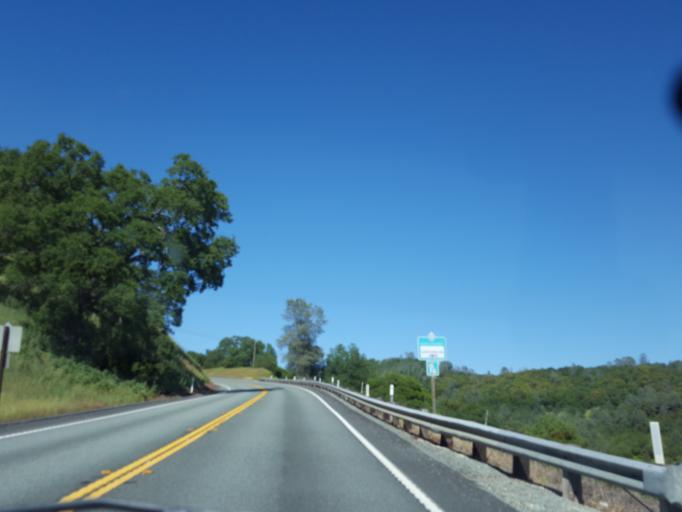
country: US
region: California
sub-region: Calaveras County
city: San Andreas
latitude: 38.2581
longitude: -120.7157
